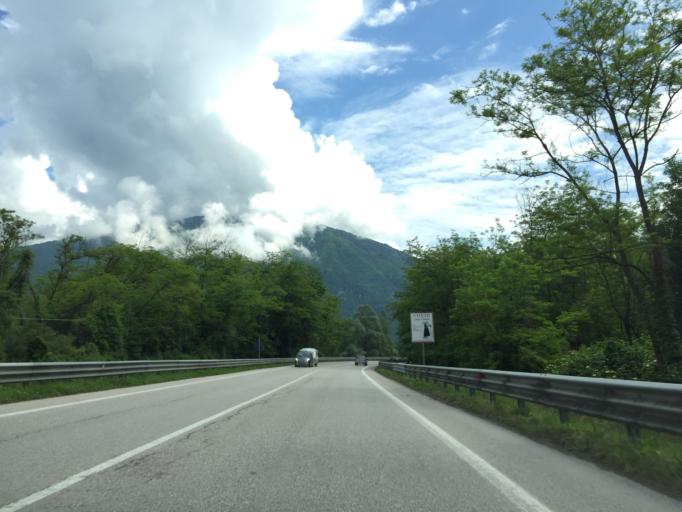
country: IT
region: Veneto
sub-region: Provincia di Belluno
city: Fonzaso
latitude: 45.9920
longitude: 11.7916
